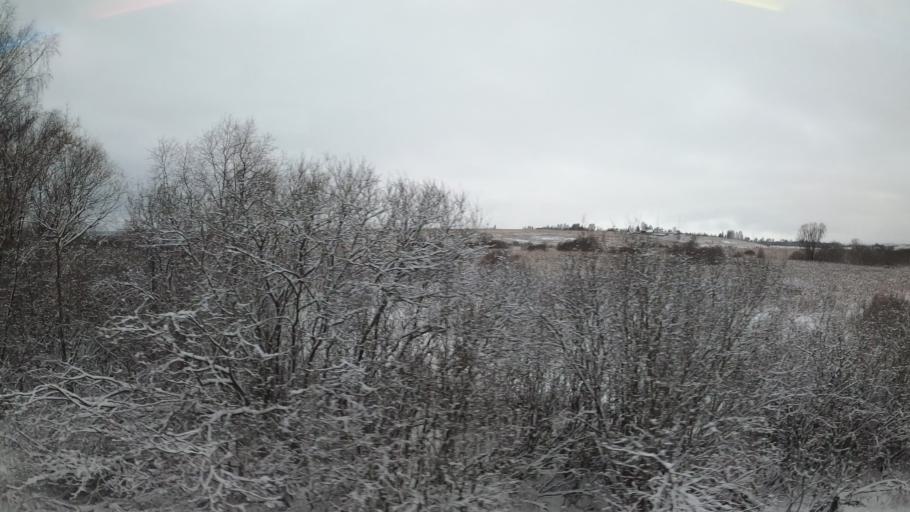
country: RU
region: Jaroslavl
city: Pereslavl'-Zalesskiy
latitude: 56.6948
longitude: 38.9169
